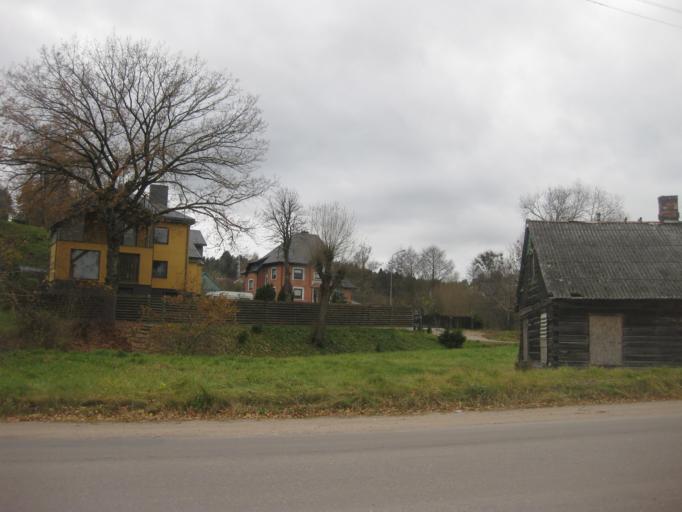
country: LT
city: Prienai
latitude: 54.6367
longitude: 23.9424
